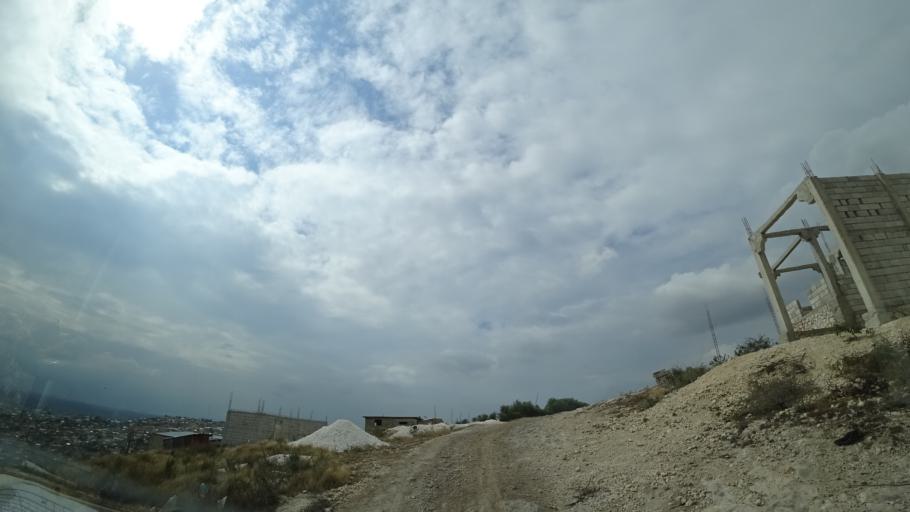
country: HT
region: Ouest
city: Croix des Bouquets
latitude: 18.6646
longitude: -72.2626
